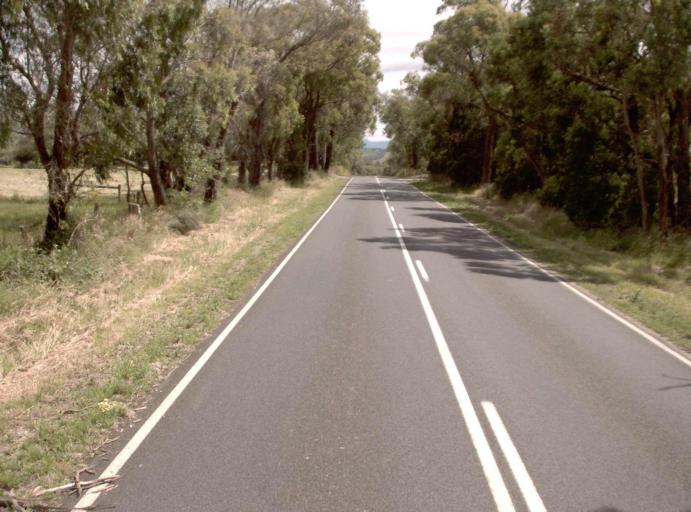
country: AU
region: Victoria
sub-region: Latrobe
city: Moe
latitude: -38.0982
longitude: 146.1573
